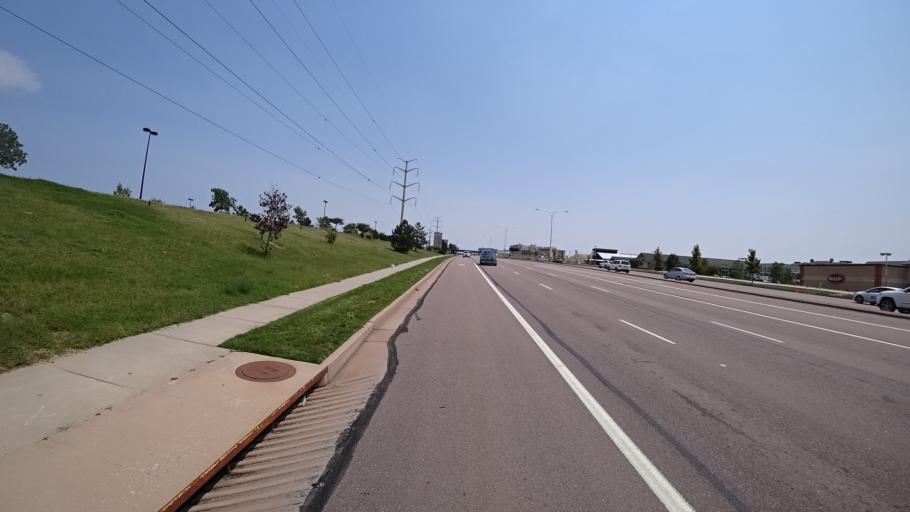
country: US
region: Colorado
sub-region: El Paso County
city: Black Forest
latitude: 38.9403
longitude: -104.7287
